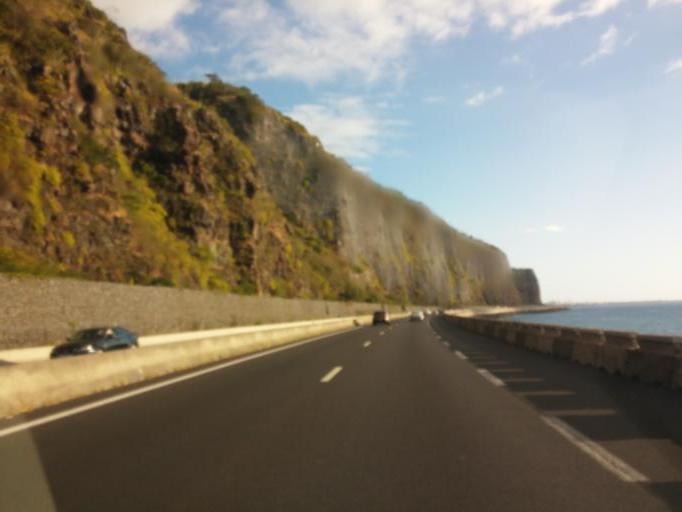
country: RE
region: Reunion
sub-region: Reunion
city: La Possession
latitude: -20.9052
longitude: 55.3640
